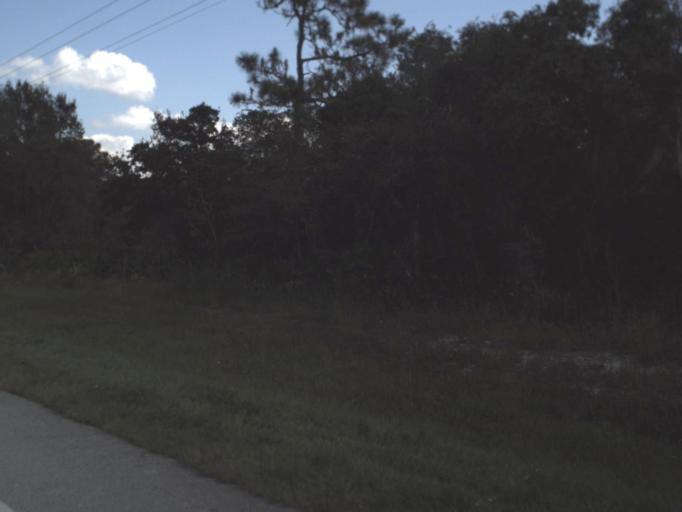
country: US
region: Florida
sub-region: Highlands County
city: Sebring
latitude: 27.4238
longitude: -81.4325
